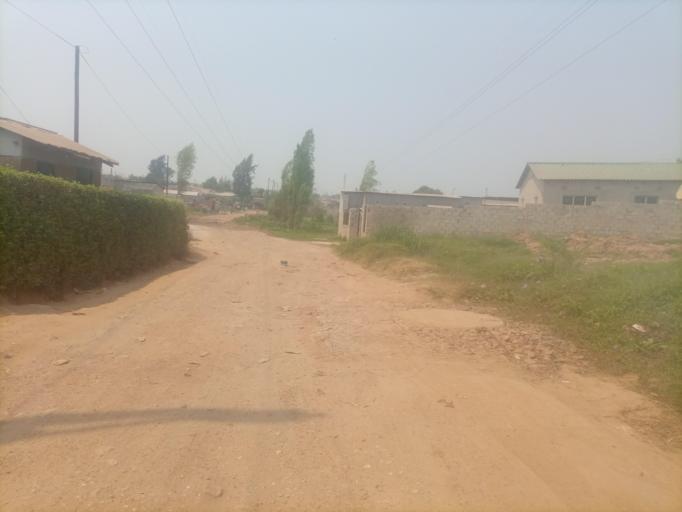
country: ZM
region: Lusaka
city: Lusaka
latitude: -15.3935
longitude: 28.3675
